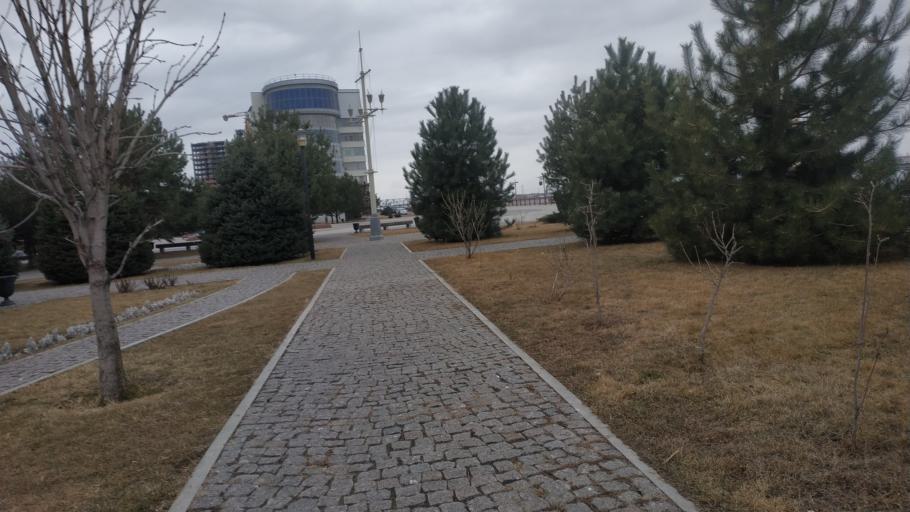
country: RU
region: Astrakhan
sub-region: Gorod Astrakhan'
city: Astrakhan'
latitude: 46.3476
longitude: 48.0167
